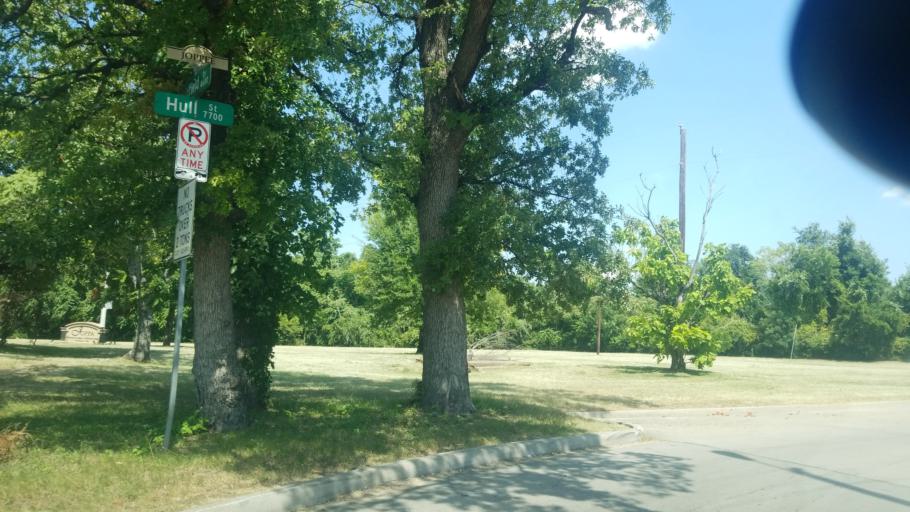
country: US
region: Texas
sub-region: Dallas County
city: Hutchins
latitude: 32.7182
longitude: -96.7500
